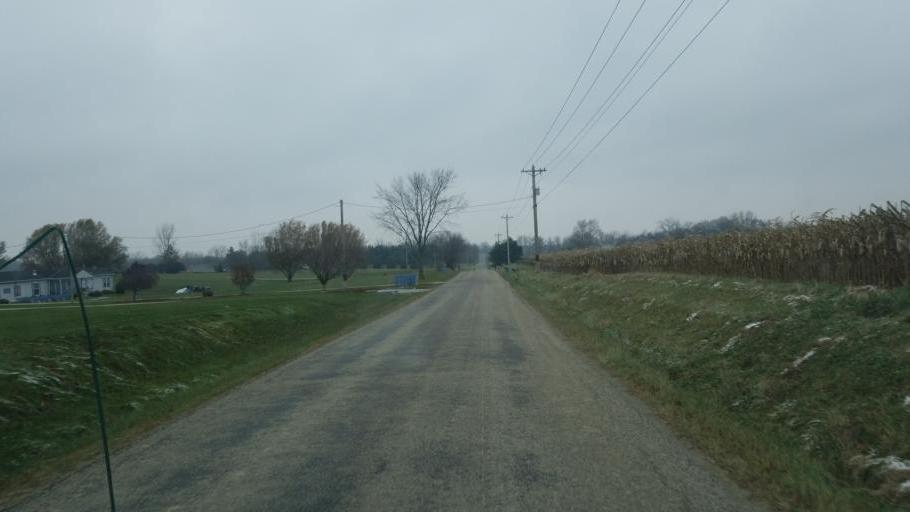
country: US
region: Ohio
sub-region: Huron County
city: New London
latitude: 41.0499
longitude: -82.3263
